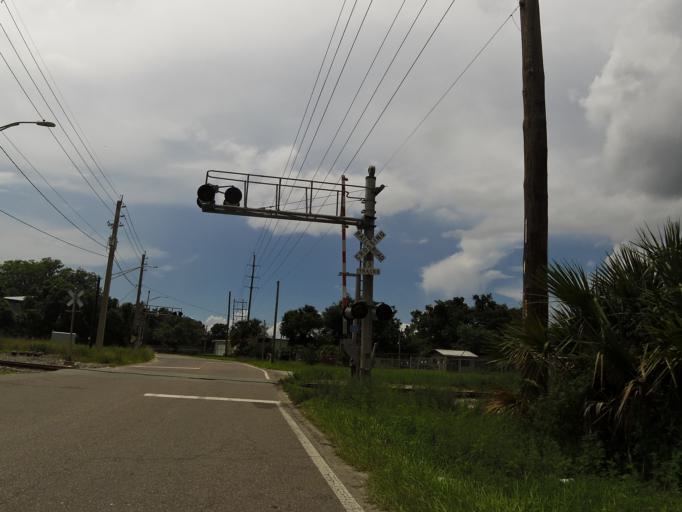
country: US
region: Florida
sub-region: Duval County
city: Jacksonville
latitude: 30.3679
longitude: -81.6371
